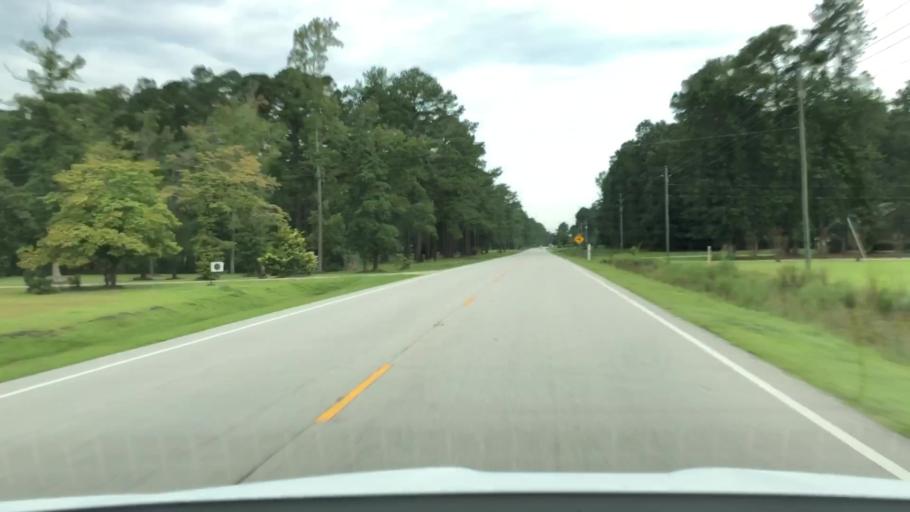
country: US
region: North Carolina
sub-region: Jones County
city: Trenton
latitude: 35.0721
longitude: -77.3792
